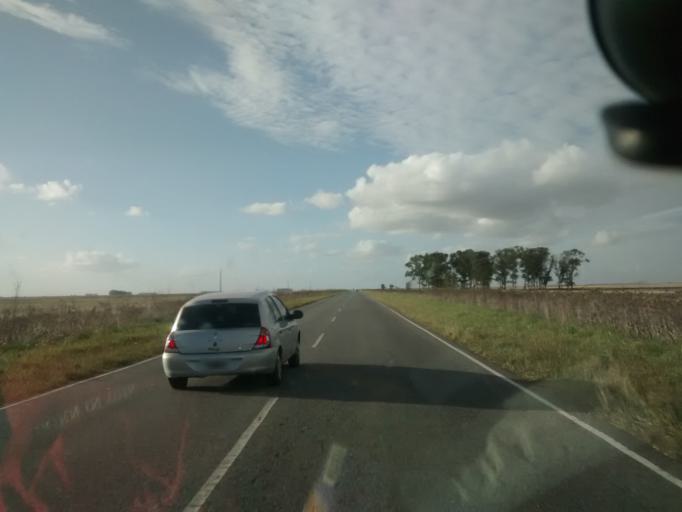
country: AR
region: Buenos Aires
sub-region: Partido de Rauch
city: Rauch
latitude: -36.4407
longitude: -58.5792
